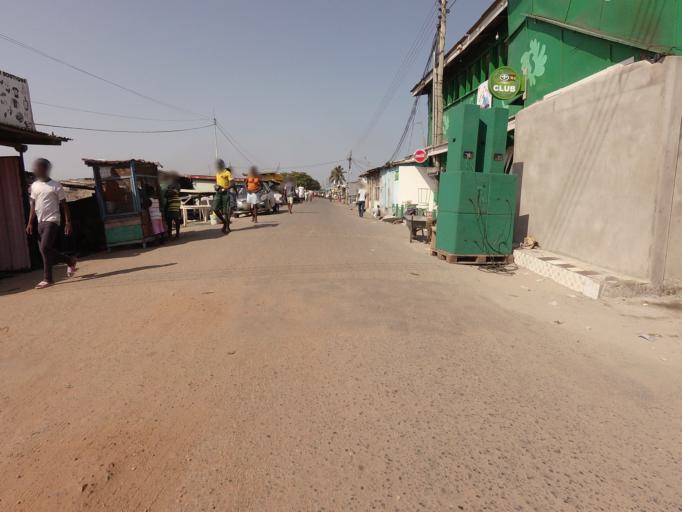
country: GH
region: Greater Accra
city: Teshi Old Town
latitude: 5.5780
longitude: -0.1055
